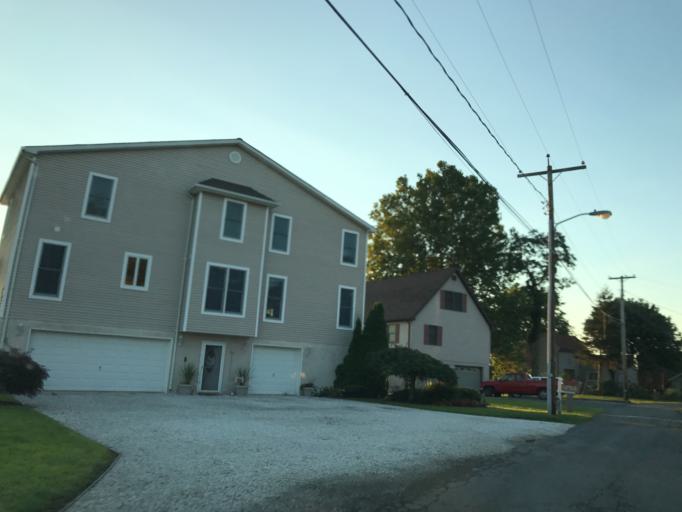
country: US
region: Maryland
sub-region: Baltimore County
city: Bowleys Quarters
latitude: 39.3288
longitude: -76.4051
